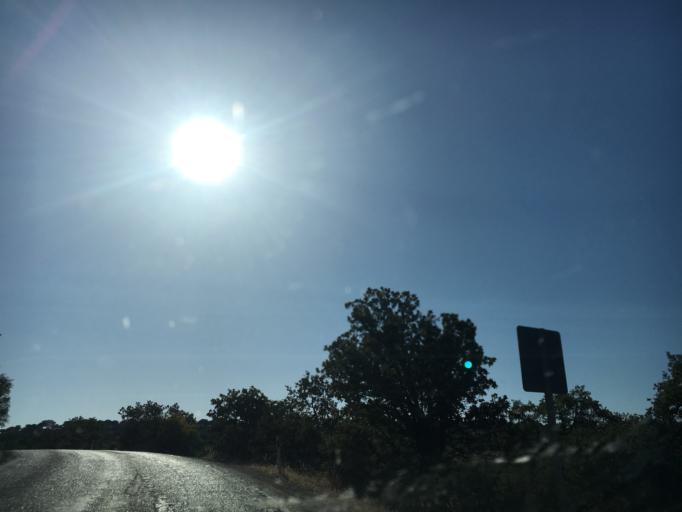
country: TR
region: Canakkale
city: Behram
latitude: 39.5004
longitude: 26.2881
